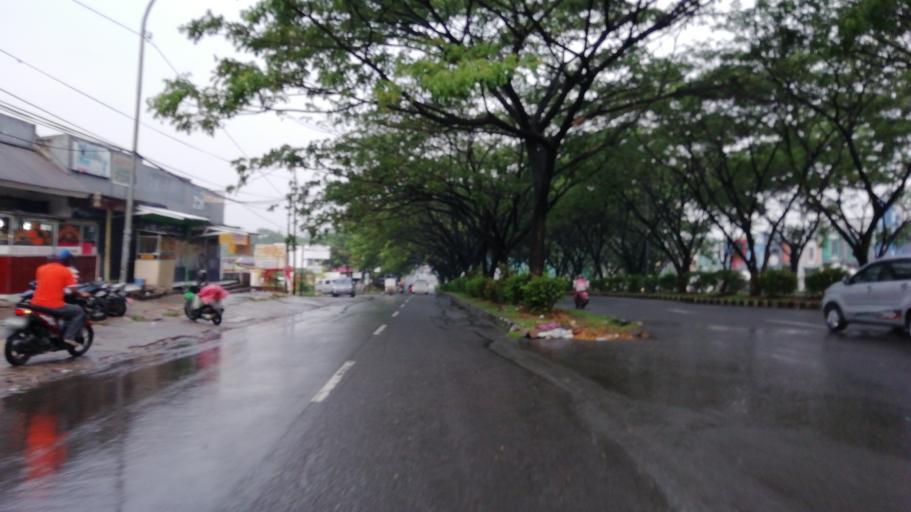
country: ID
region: West Java
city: Cibinong
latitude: -6.4820
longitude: 106.8125
